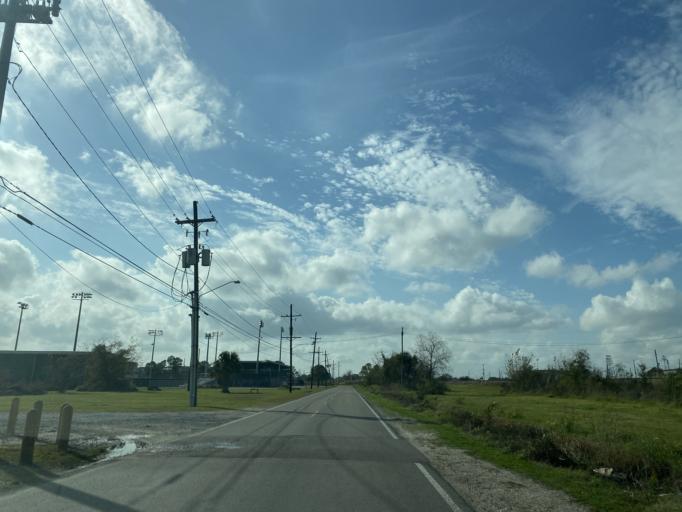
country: US
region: Louisiana
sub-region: Orleans Parish
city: New Orleans
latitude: 30.0295
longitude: -90.0406
